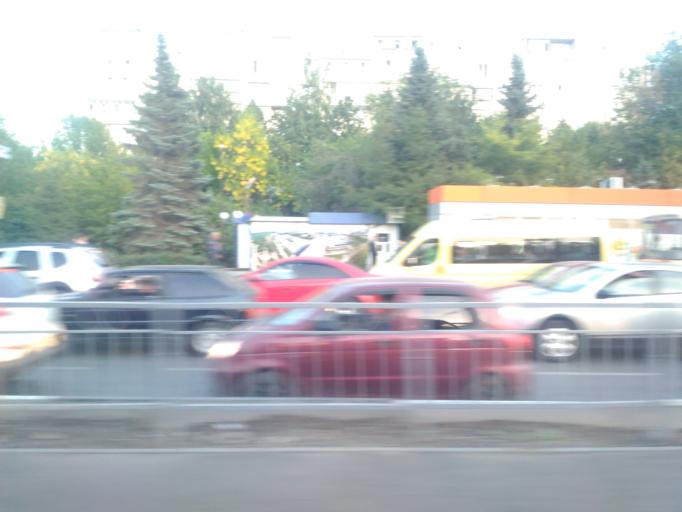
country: RU
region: Ulyanovsk
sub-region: Ulyanovskiy Rayon
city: Ulyanovsk
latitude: 54.2800
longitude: 48.2959
